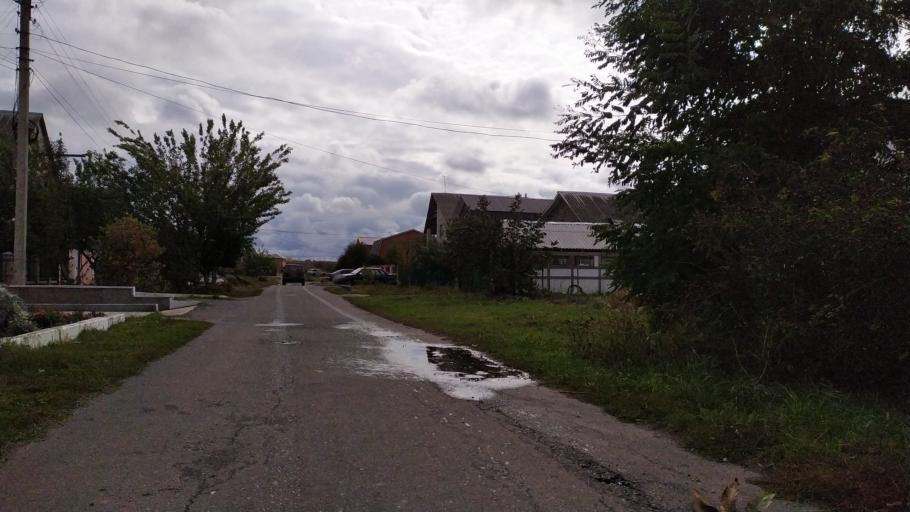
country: RU
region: Kursk
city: Kursk
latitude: 51.6430
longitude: 36.1552
